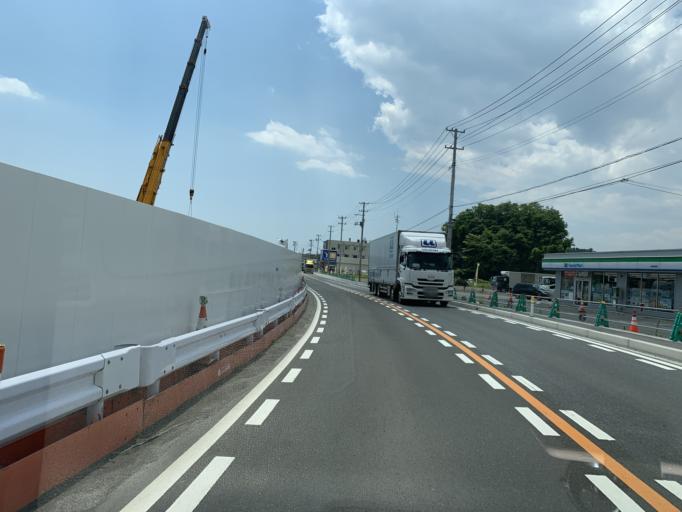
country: JP
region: Miyagi
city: Matsushima
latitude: 38.3823
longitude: 141.0676
